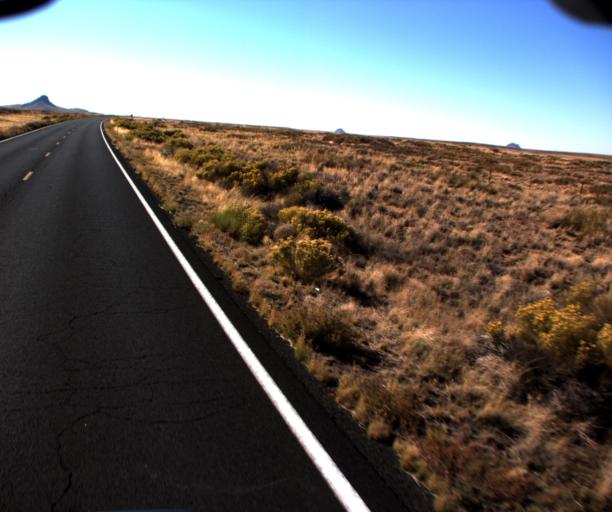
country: US
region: Arizona
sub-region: Navajo County
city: Dilkon
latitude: 35.4640
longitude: -110.4225
